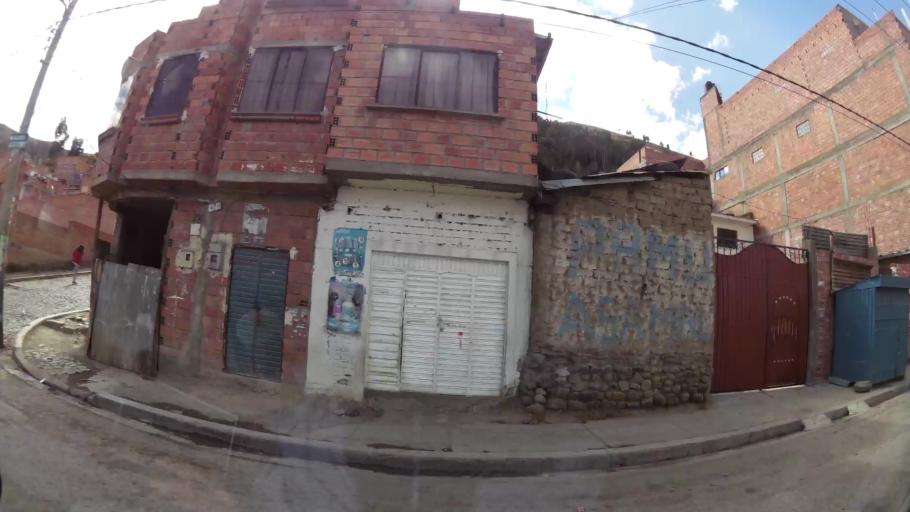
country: BO
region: La Paz
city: La Paz
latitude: -16.4655
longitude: -68.1156
